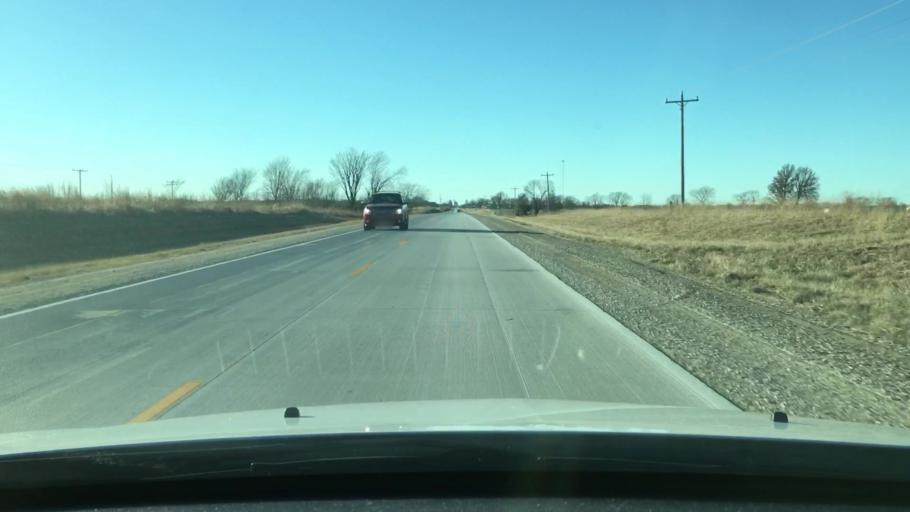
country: US
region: Missouri
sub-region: Boone County
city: Centralia
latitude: 39.2035
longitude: -92.0779
